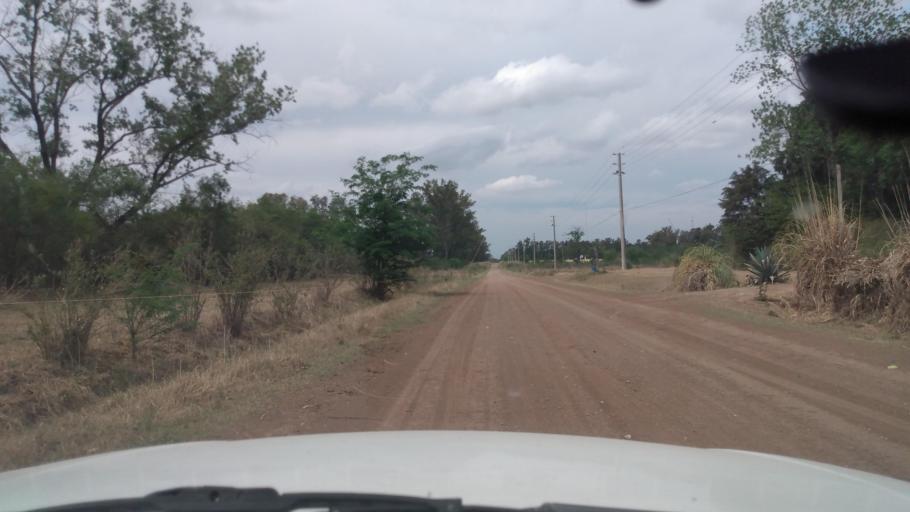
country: AR
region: Buenos Aires
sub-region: Partido de Lujan
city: Lujan
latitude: -34.5564
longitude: -59.1797
